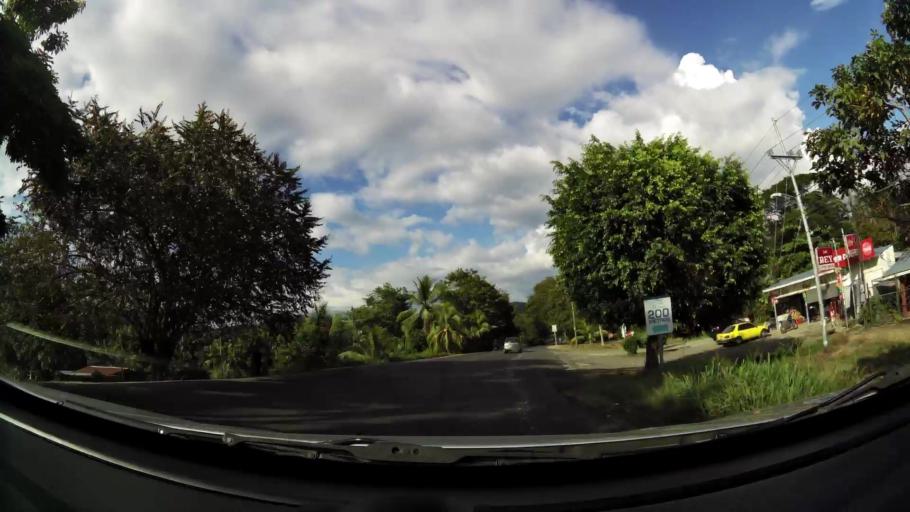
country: CR
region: Puntarenas
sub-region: Canton de Garabito
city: Jaco
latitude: 9.6650
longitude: -84.6400
